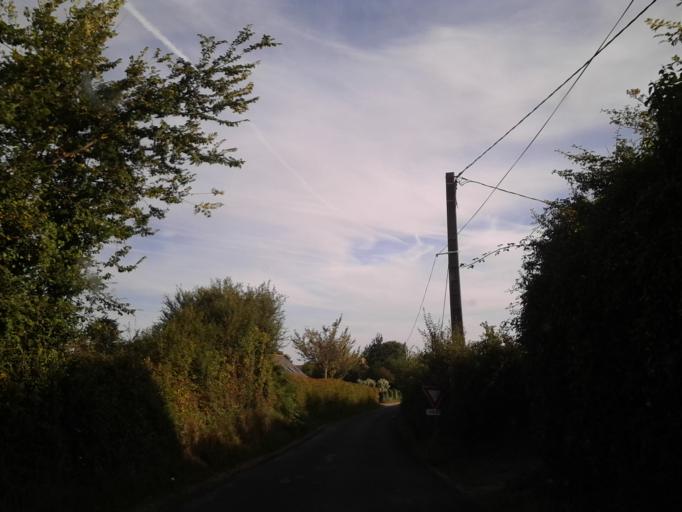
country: FR
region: Lower Normandy
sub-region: Departement de la Manche
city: Fermanville
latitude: 49.6801
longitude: -1.4556
